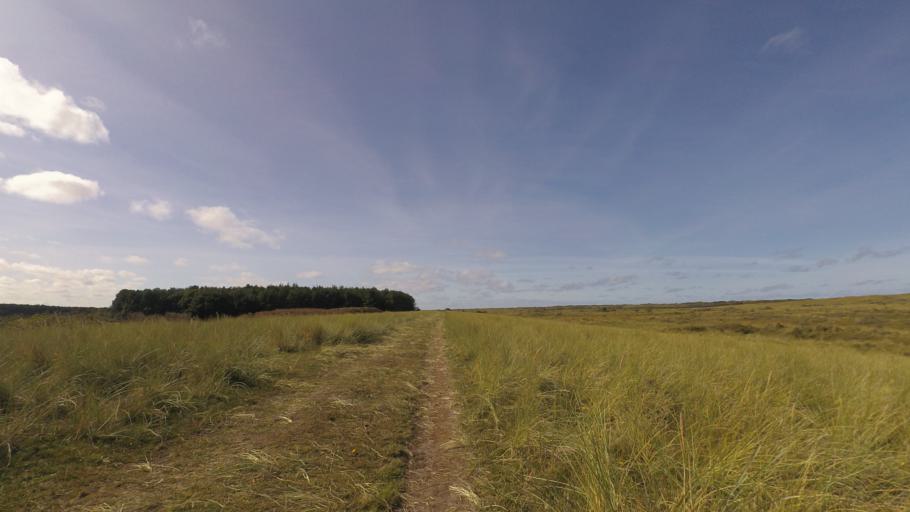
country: NL
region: Friesland
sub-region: Gemeente Ameland
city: Nes
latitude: 53.4517
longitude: 5.7202
